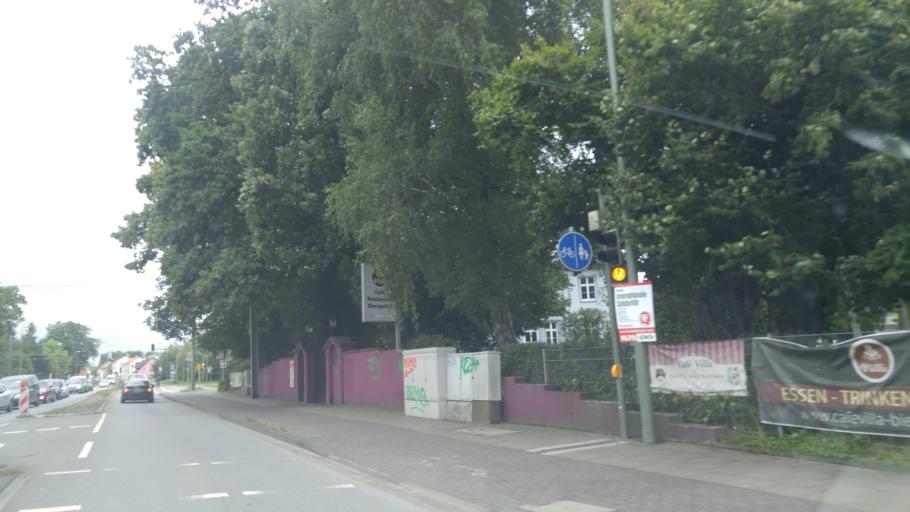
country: DE
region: North Rhine-Westphalia
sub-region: Regierungsbezirk Detmold
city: Bielefeld
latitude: 52.0408
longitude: 8.5440
